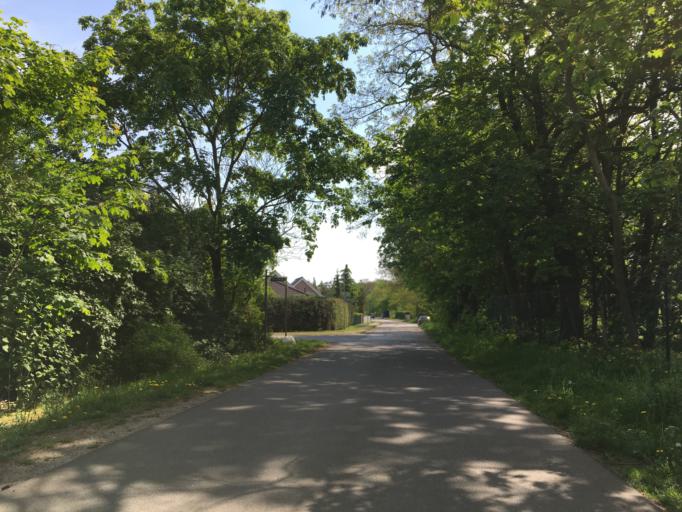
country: DE
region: Brandenburg
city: Werneuchen
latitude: 52.6004
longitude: 13.7443
